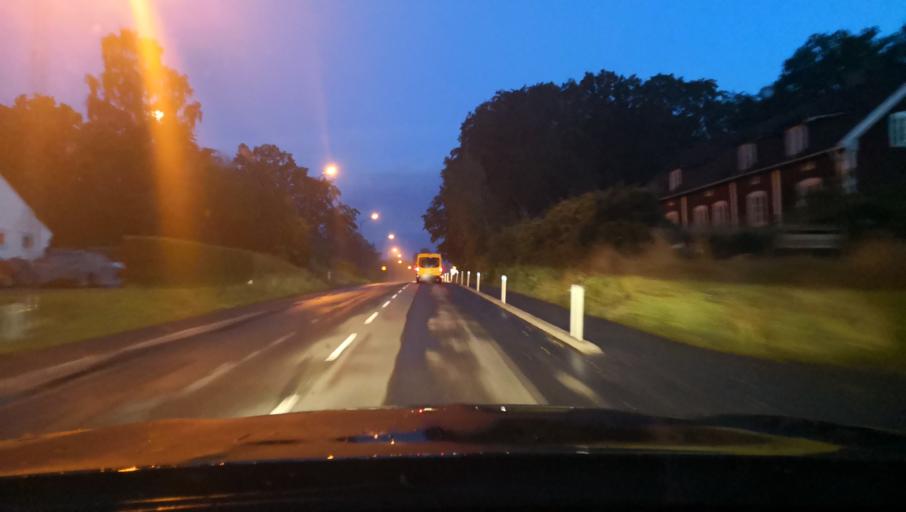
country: SE
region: Skane
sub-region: Osby Kommun
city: Osby
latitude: 56.3649
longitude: 13.9816
